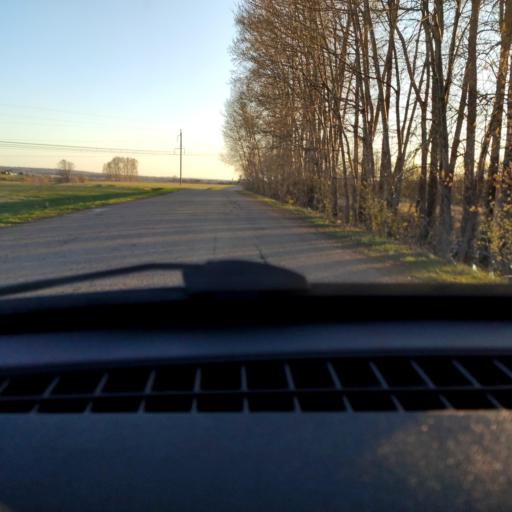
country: RU
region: Bashkortostan
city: Avdon
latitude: 54.4909
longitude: 55.6044
